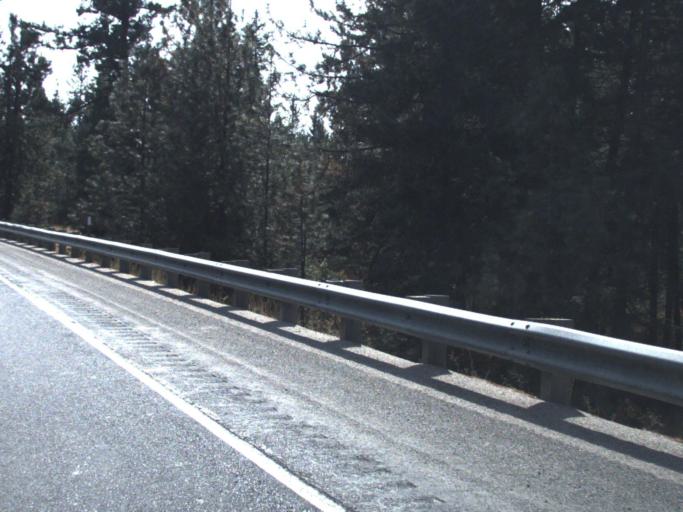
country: US
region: Washington
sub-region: Spokane County
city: Deer Park
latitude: 48.0336
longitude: -117.6045
